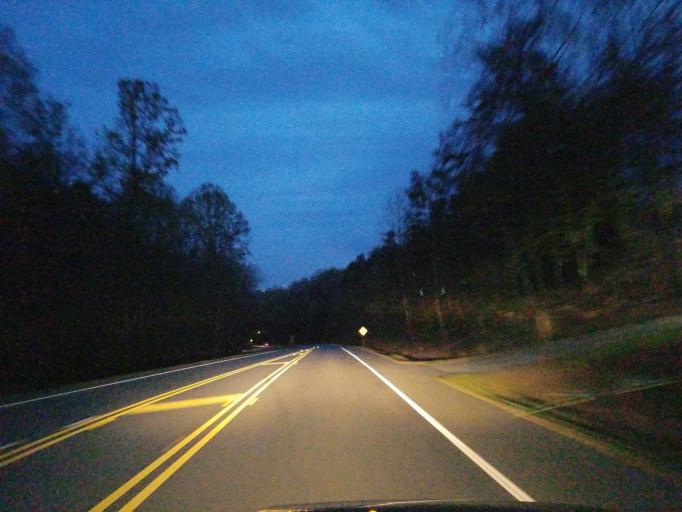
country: US
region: Georgia
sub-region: Lumpkin County
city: Dahlonega
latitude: 34.5619
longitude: -83.9665
